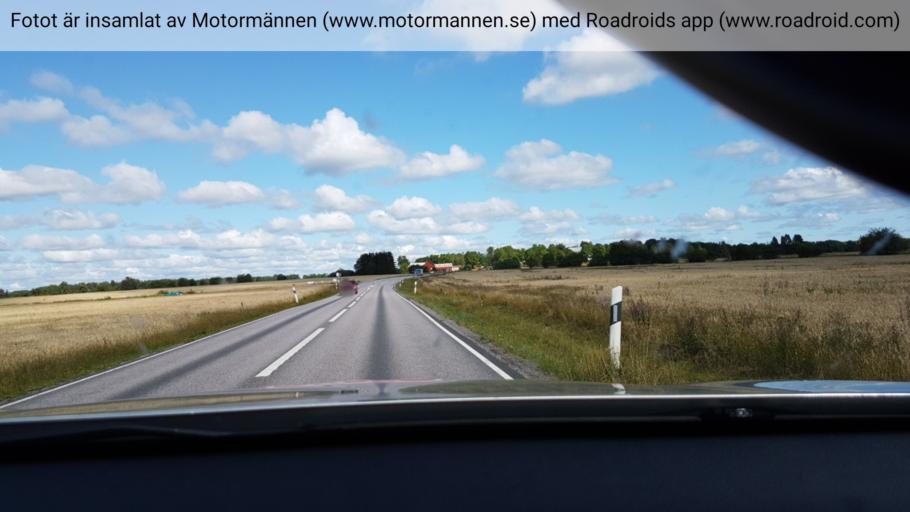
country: SE
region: Stockholm
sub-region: Norrtalje Kommun
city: Norrtalje
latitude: 59.8105
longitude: 18.6494
